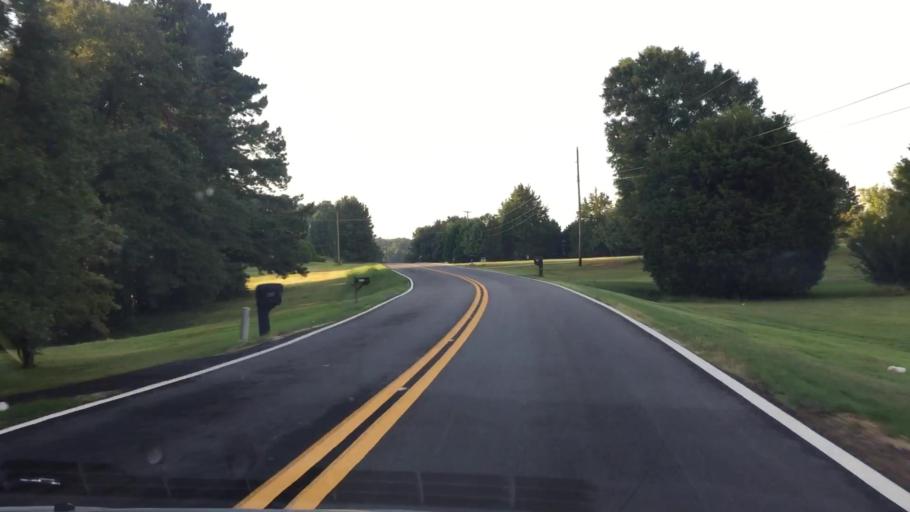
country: US
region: Georgia
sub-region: Henry County
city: McDonough
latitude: 33.4626
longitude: -84.1925
